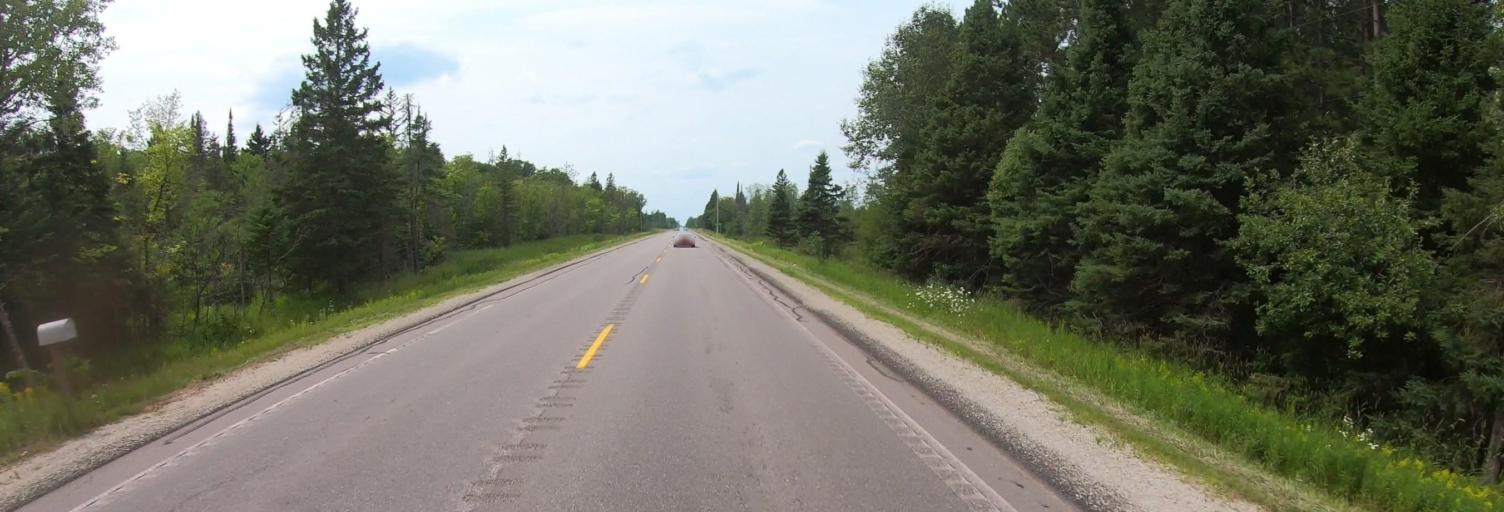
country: US
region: Michigan
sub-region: Marquette County
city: K. I. Sawyer Air Force Base
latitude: 46.3476
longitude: -87.1532
